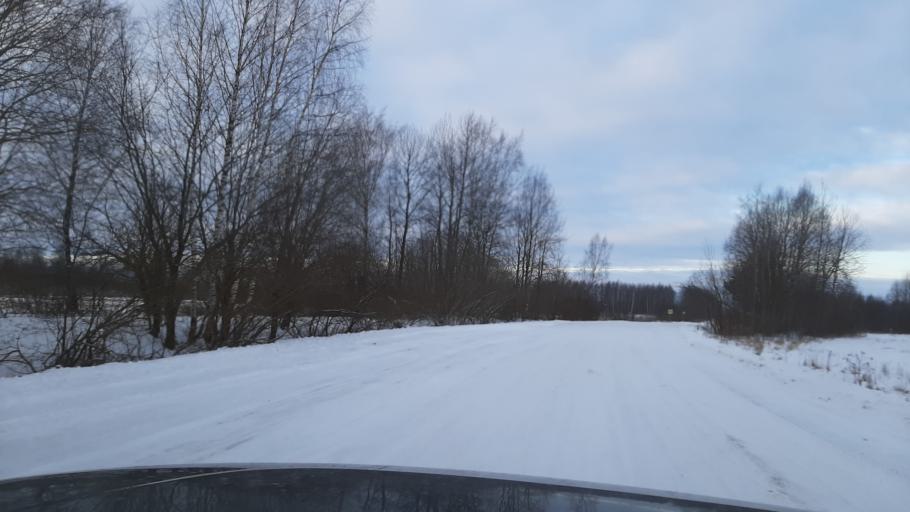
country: RU
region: Kostroma
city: Kosmynino
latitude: 57.4793
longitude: 40.8514
